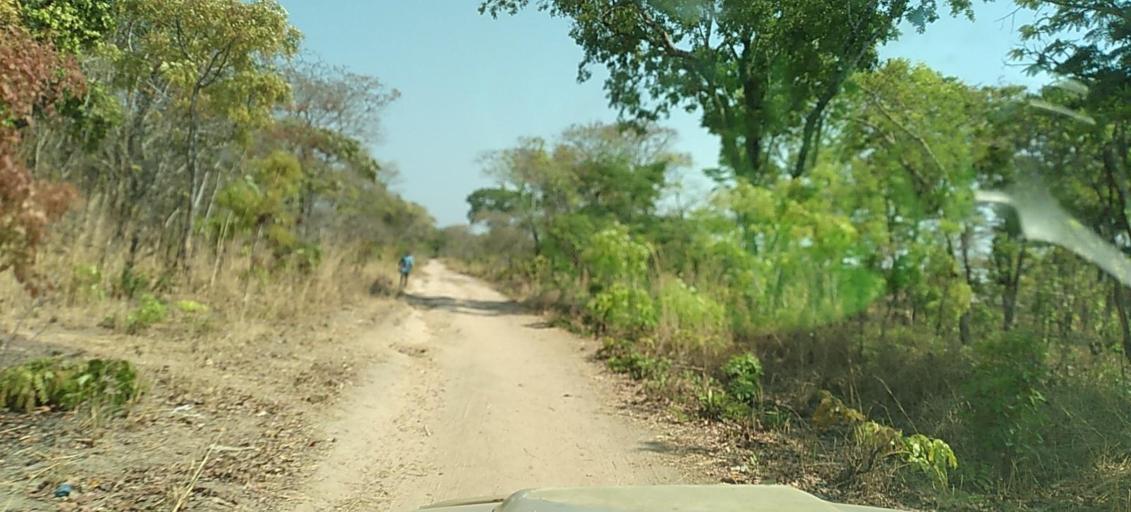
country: ZM
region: North-Western
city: Kalengwa
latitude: -13.3029
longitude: 24.7987
